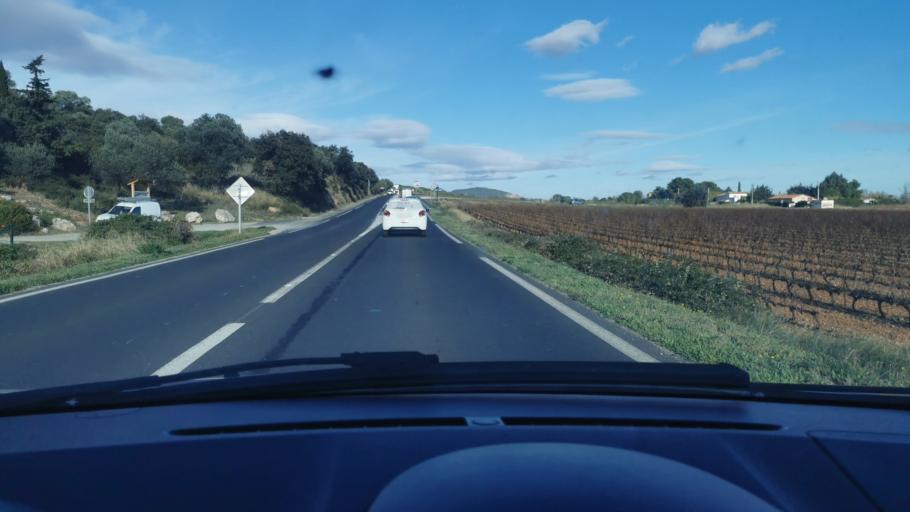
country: FR
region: Languedoc-Roussillon
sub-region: Departement de l'Herault
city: Vic-la-Gardiole
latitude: 43.4901
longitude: 3.7734
